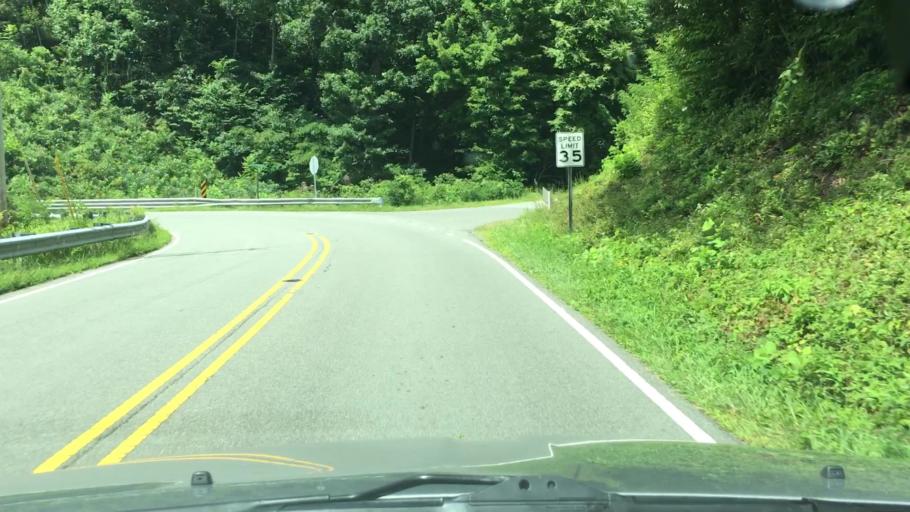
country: US
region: North Carolina
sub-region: Yancey County
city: Burnsville
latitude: 35.7948
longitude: -82.2013
